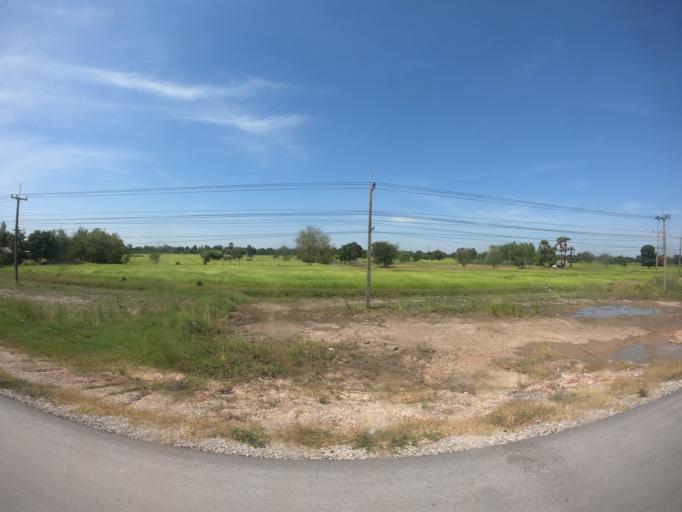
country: TH
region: Nakhon Ratchasima
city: Sida
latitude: 15.5736
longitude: 102.5543
